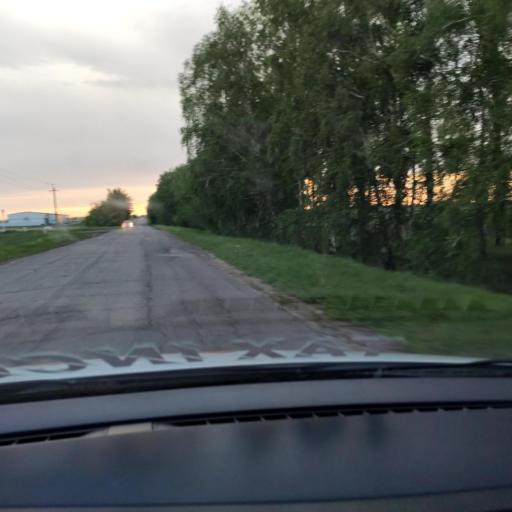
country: RU
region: Voronezj
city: Maslovka
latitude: 51.4434
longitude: 39.2642
